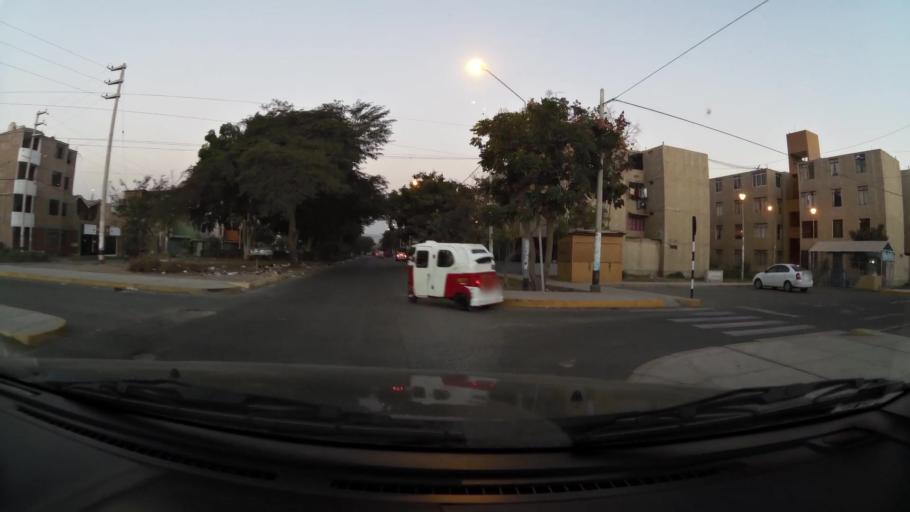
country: PE
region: Ica
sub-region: Provincia de Ica
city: Ica
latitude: -14.0837
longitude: -75.7282
